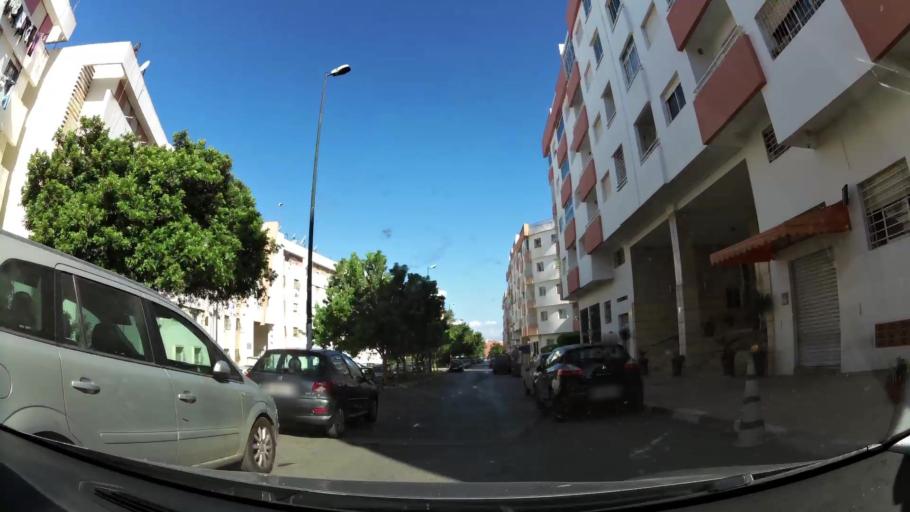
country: MA
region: Rabat-Sale-Zemmour-Zaer
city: Sale
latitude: 34.0683
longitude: -6.7937
